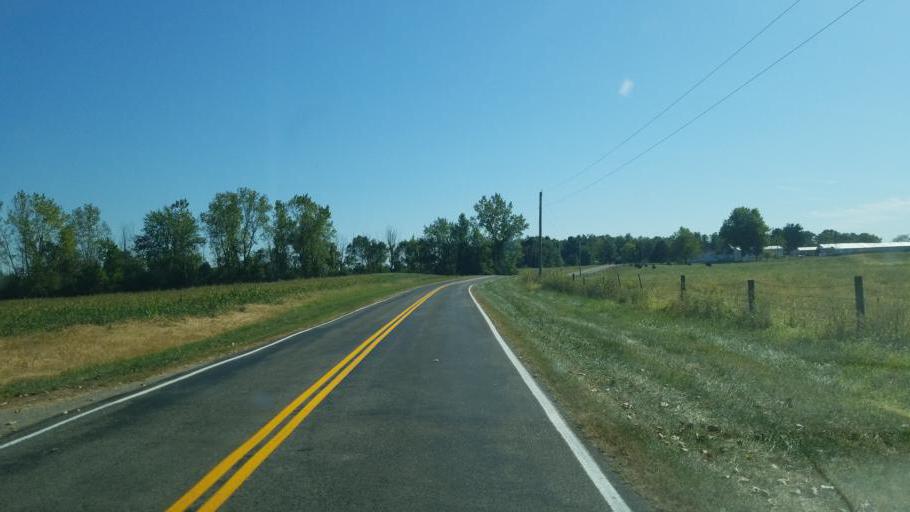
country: US
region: Ohio
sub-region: Champaign County
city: North Lewisburg
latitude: 40.1527
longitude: -83.6000
